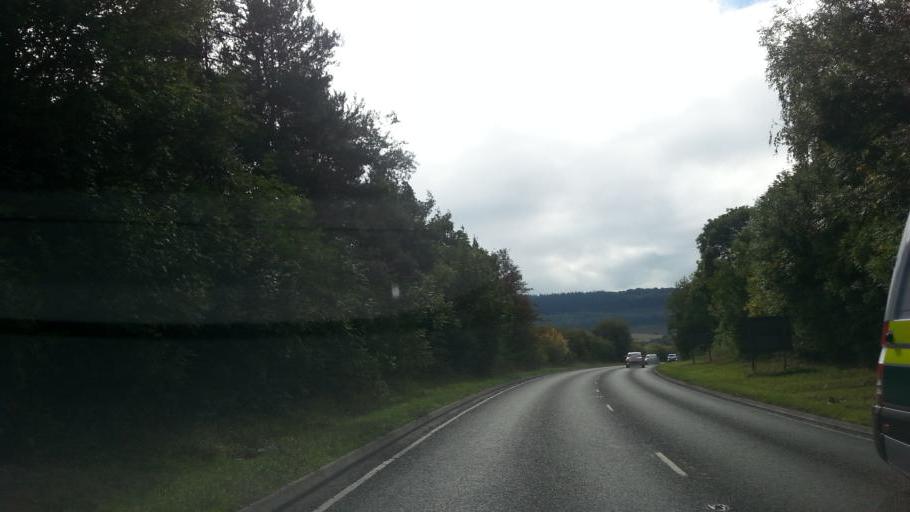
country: GB
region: England
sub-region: Herefordshire
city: Ross on Wye
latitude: 51.9255
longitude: -2.5712
